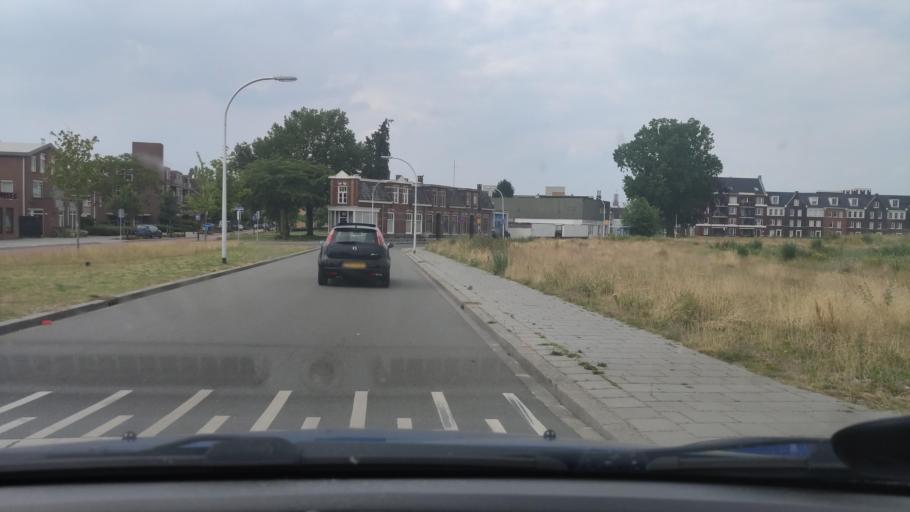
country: NL
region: Overijssel
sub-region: Gemeente Hengelo
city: Hengelo
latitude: 52.2579
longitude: 6.8016
